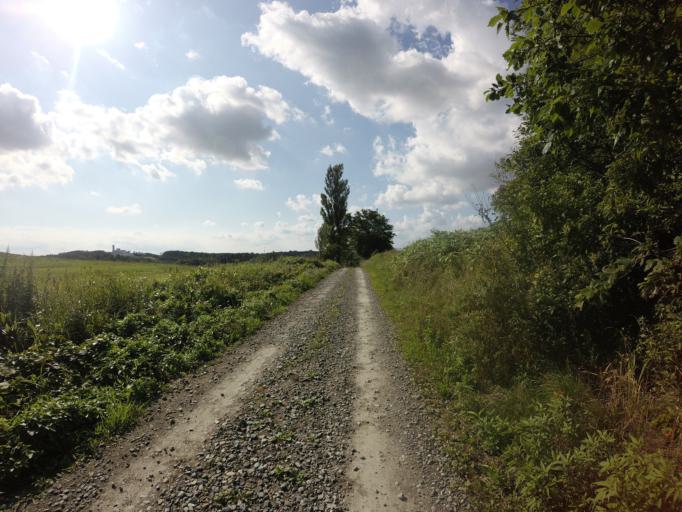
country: JP
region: Hokkaido
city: Iwamizawa
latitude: 43.1938
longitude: 141.8162
